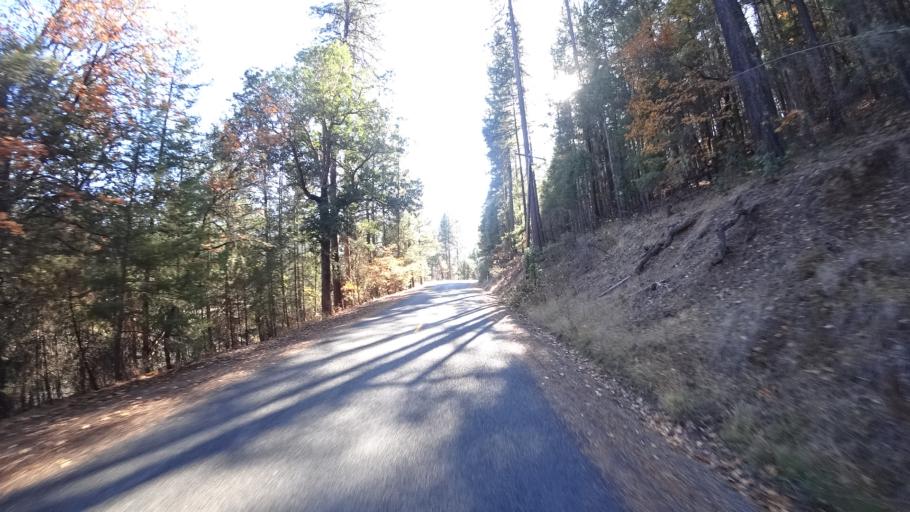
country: US
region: California
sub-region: Siskiyou County
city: Yreka
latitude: 41.8259
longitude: -122.9777
